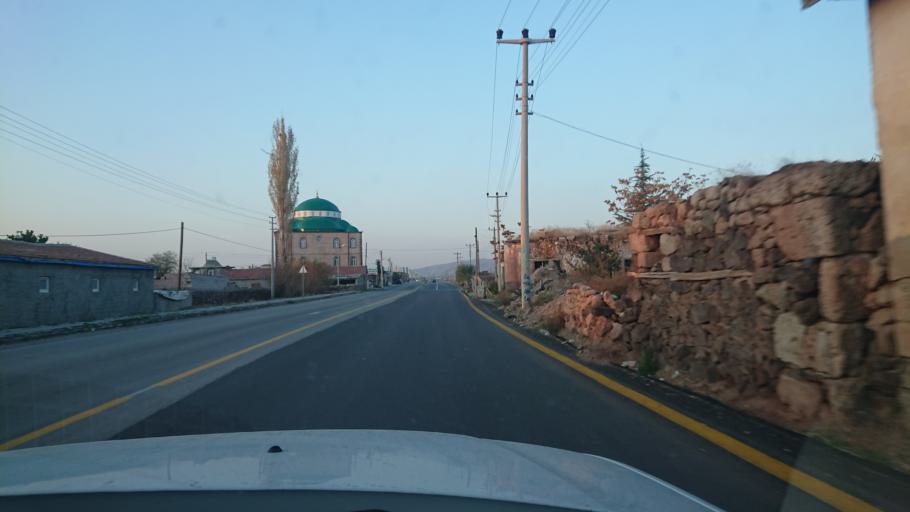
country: TR
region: Aksaray
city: Aksaray
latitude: 38.3180
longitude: 34.0531
